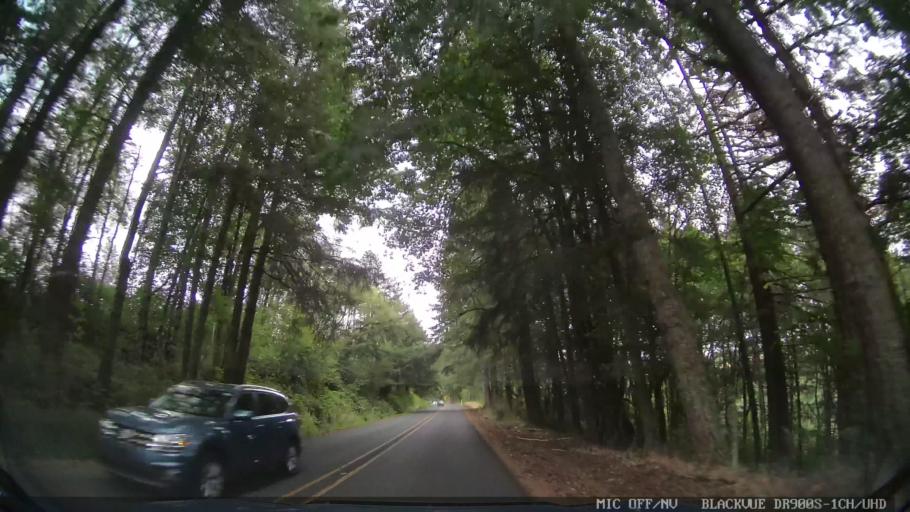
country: US
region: Oregon
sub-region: Linn County
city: Lyons
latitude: 44.8487
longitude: -122.6720
